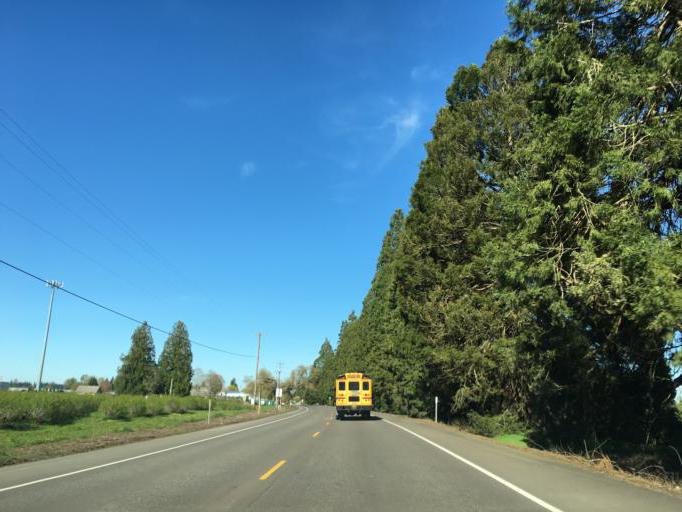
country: US
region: Oregon
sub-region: Marion County
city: Hubbard
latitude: 45.2172
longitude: -122.7643
